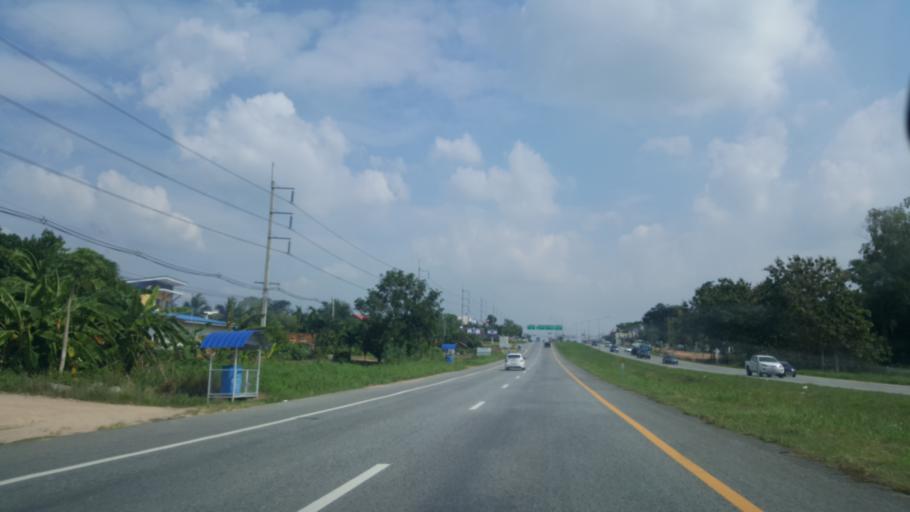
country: TH
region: Chon Buri
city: Ban Talat Bueng
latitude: 12.9484
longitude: 101.0451
